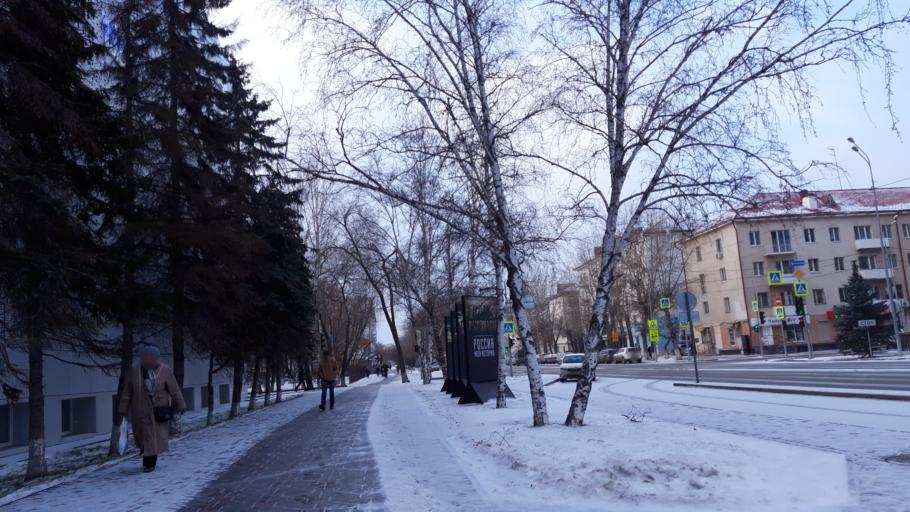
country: RU
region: Tjumen
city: Tyumen
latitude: 57.1531
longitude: 65.5482
